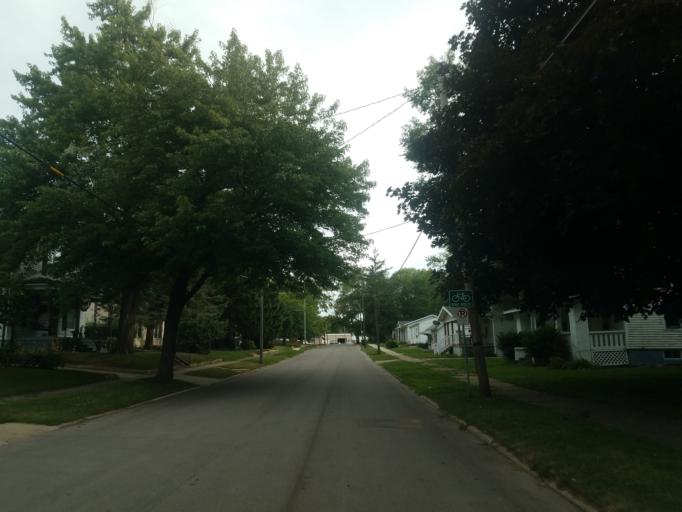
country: US
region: Illinois
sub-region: McLean County
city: Bloomington
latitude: 40.4684
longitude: -88.9855
